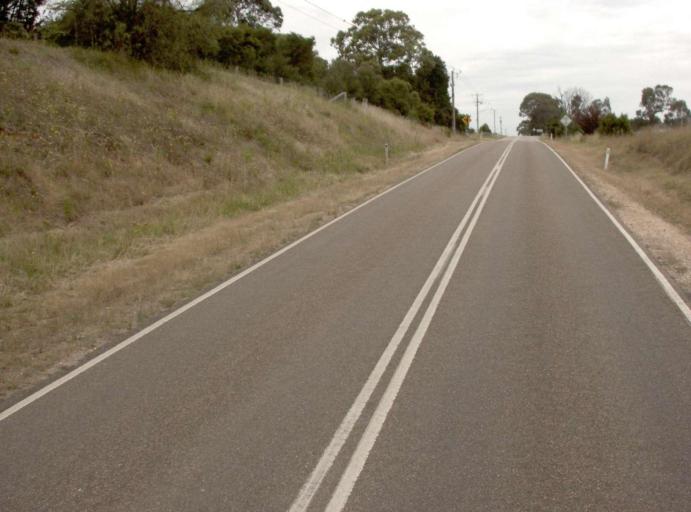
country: AU
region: Victoria
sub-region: East Gippsland
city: Bairnsdale
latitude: -37.7992
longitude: 147.4398
